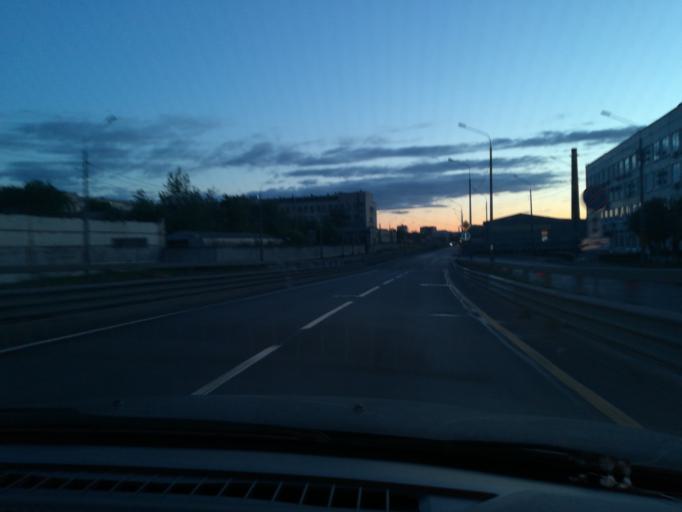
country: RU
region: St.-Petersburg
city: Avtovo
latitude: 59.8560
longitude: 30.2706
